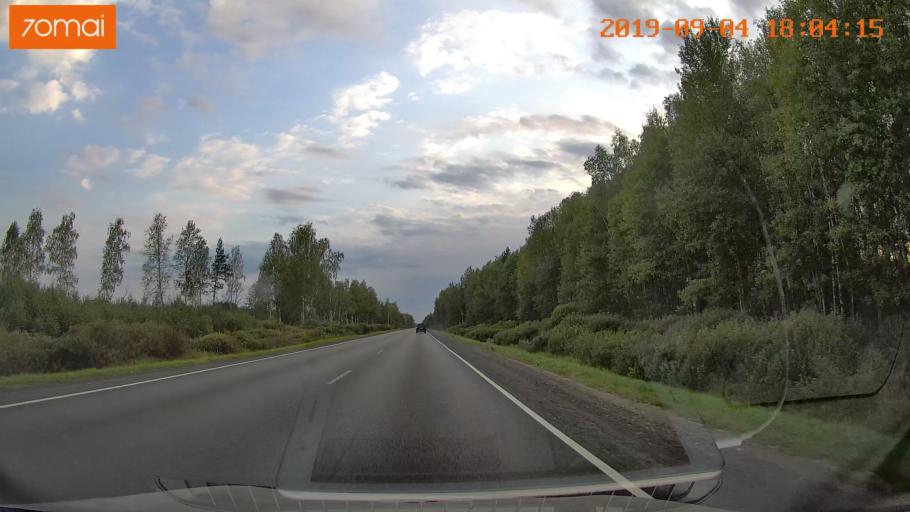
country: RU
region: Moskovskaya
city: Il'inskiy Pogost
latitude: 55.4543
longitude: 38.8415
